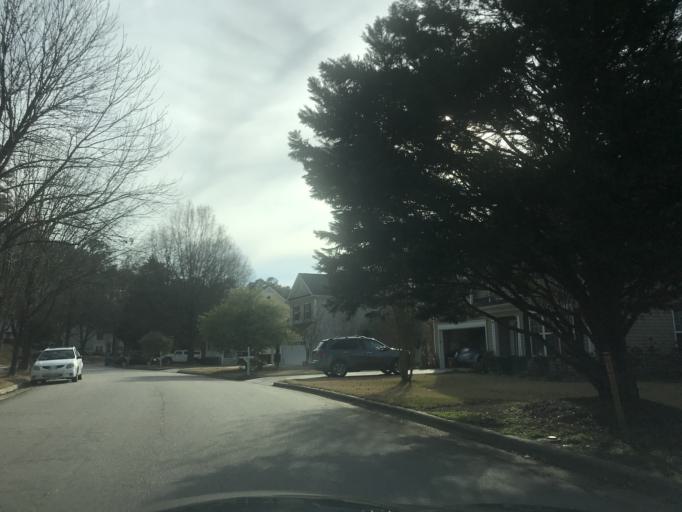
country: US
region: North Carolina
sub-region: Wake County
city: Raleigh
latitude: 35.8290
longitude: -78.5907
